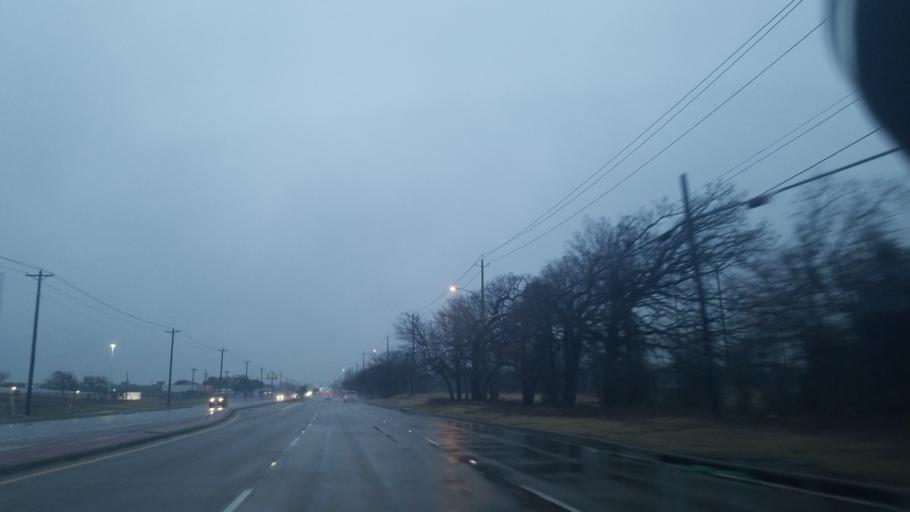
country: US
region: Texas
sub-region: Denton County
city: Denton
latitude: 33.2235
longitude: -97.0904
